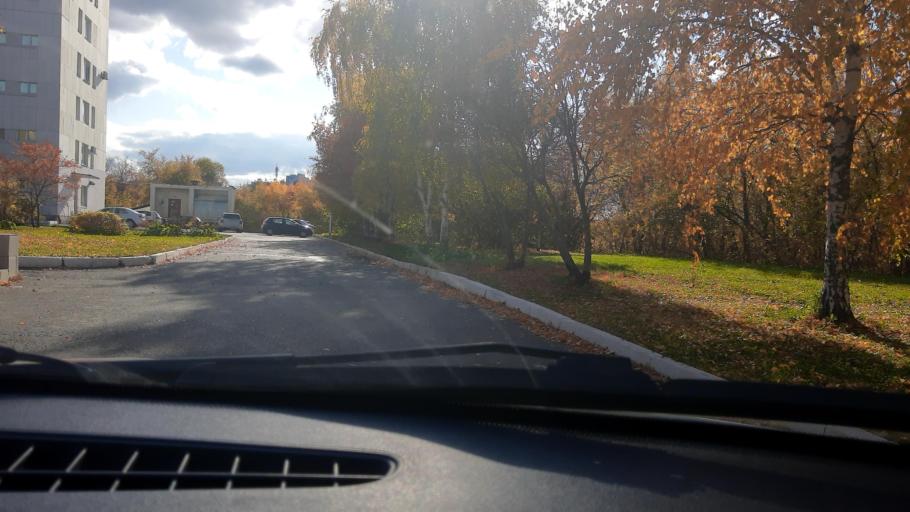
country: RU
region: Bashkortostan
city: Ufa
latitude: 54.7805
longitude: 56.0190
